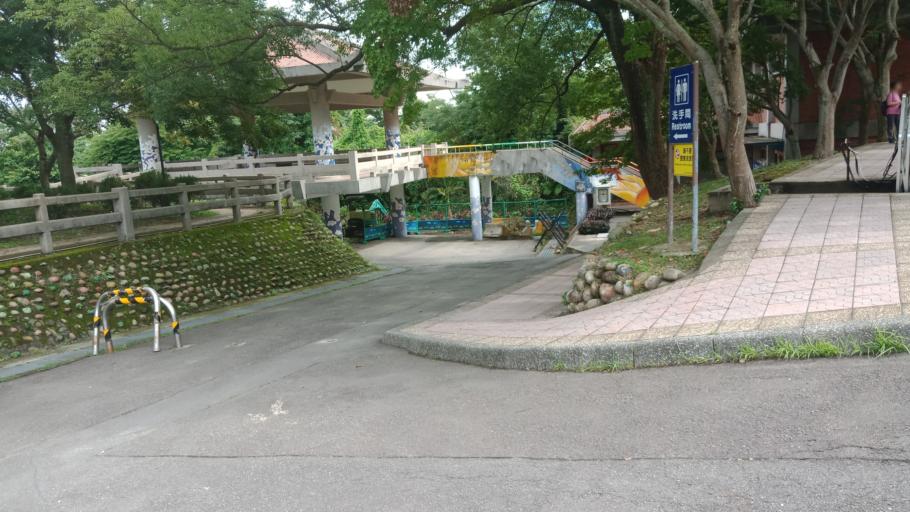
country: TW
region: Taiwan
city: Daxi
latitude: 24.8210
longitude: 121.2556
